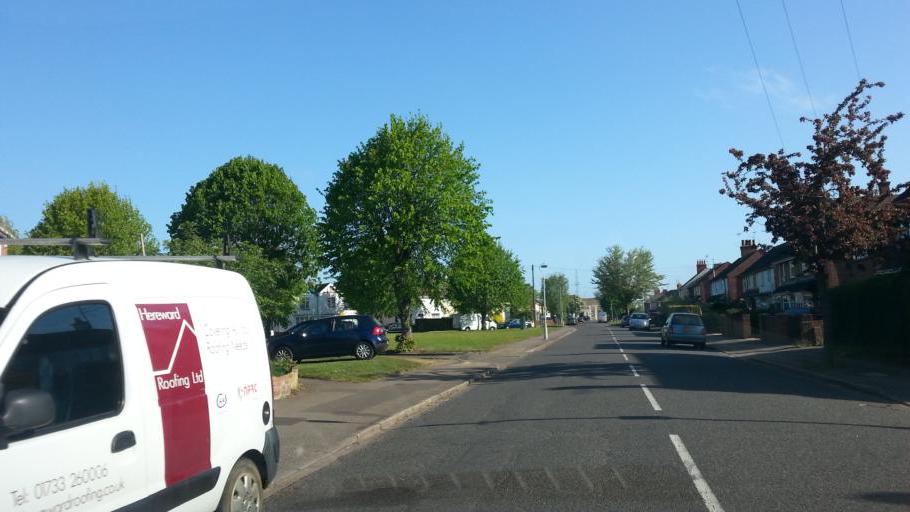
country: GB
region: England
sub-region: Peterborough
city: Peterborough
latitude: 52.5805
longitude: -0.2610
